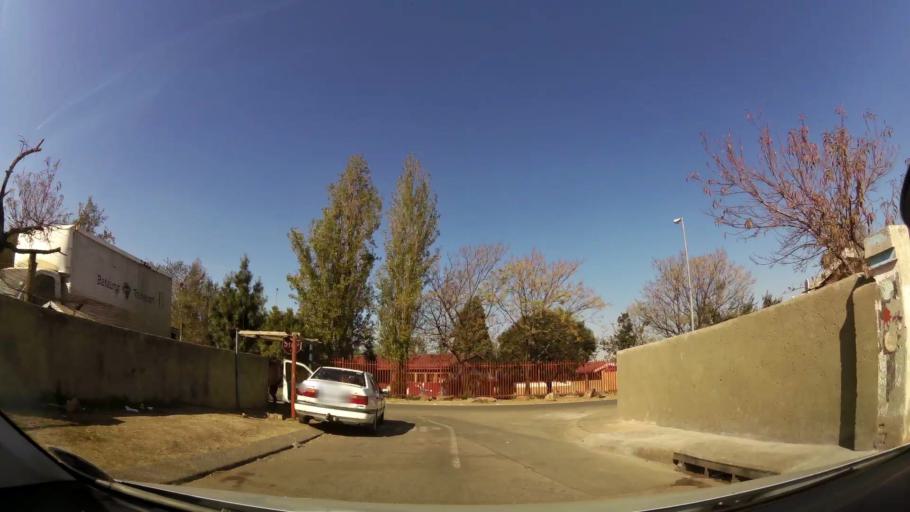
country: ZA
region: Gauteng
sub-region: City of Johannesburg Metropolitan Municipality
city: Soweto
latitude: -26.2814
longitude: 27.8672
